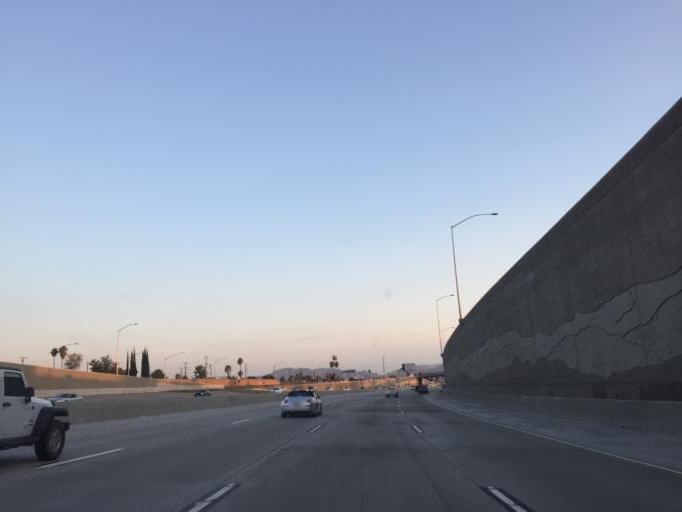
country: US
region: California
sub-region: San Bernardino County
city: San Bernardino
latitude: 34.1269
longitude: -117.3028
